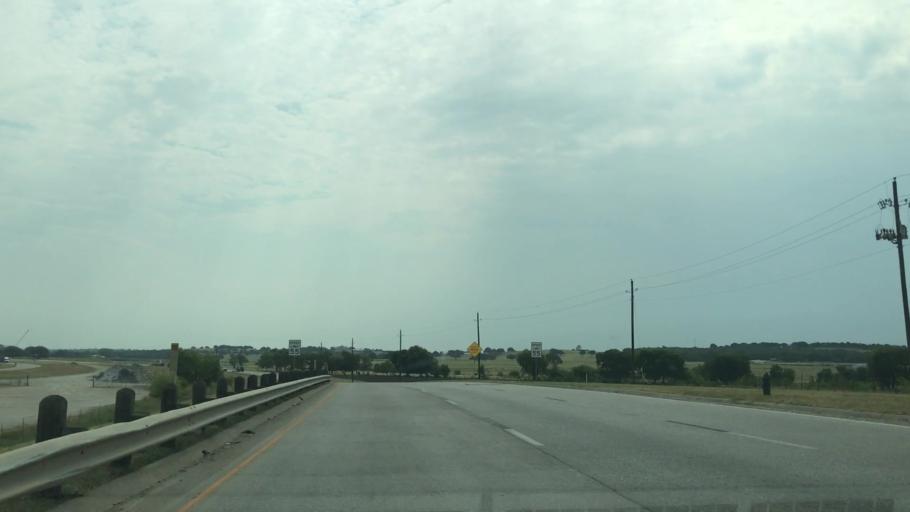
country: US
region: Texas
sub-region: Denton County
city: Roanoke
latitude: 32.9851
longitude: -97.2358
